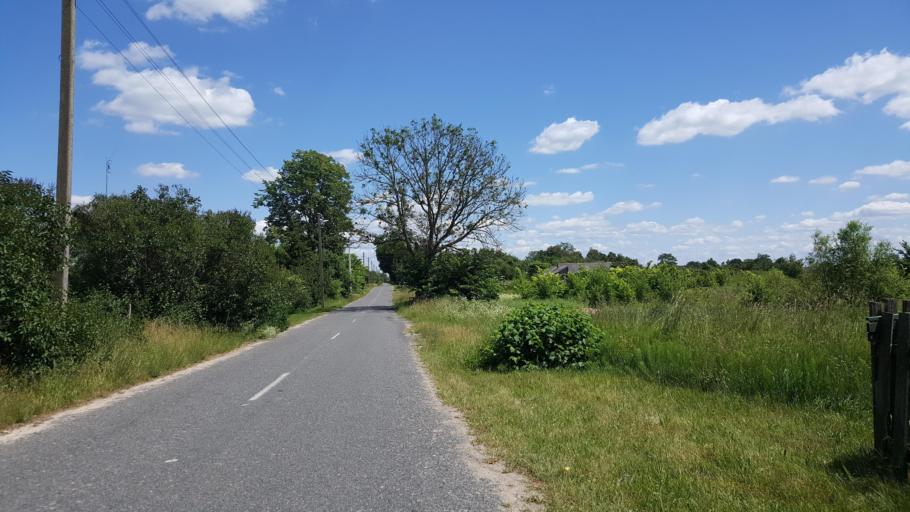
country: PL
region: Podlasie
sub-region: Powiat hajnowski
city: Czeremcha
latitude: 52.5132
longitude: 23.5423
